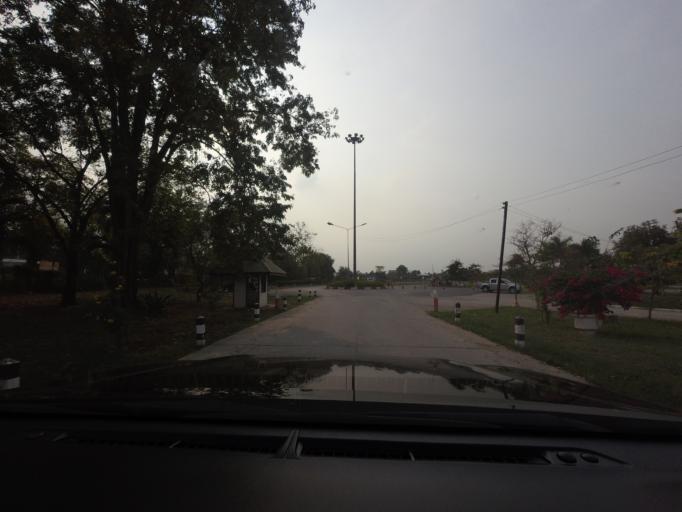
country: TH
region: Sara Buri
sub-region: Amphoe Wang Muang
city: Wang Muang
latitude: 14.8425
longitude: 101.0994
